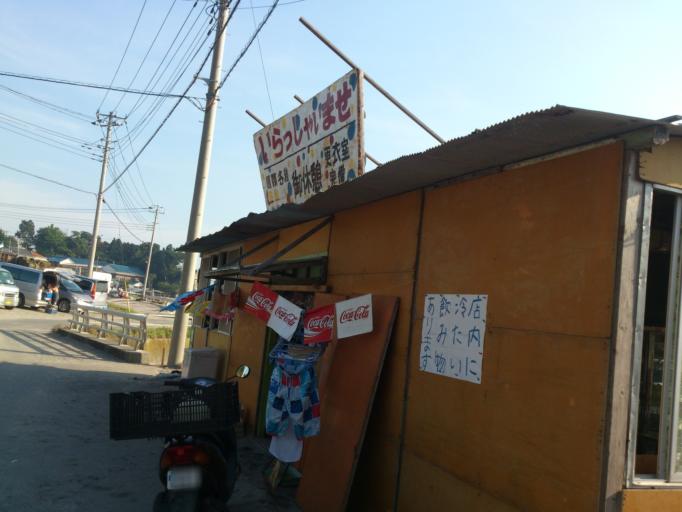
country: JP
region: Chiba
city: Tateyama
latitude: 35.0514
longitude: 139.8323
